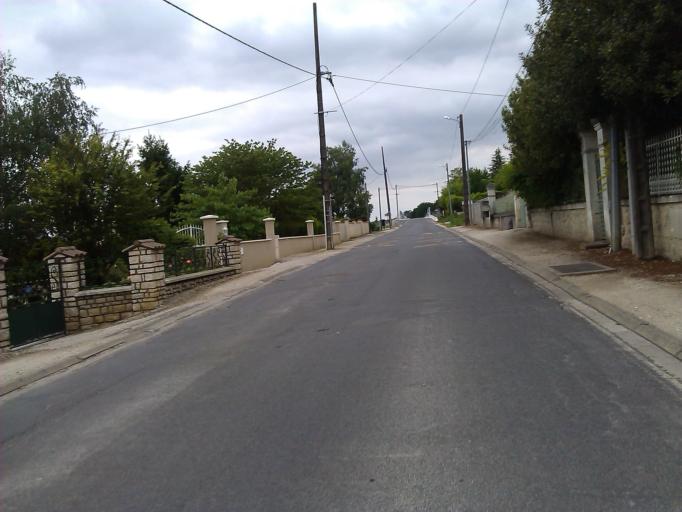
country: FR
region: Poitou-Charentes
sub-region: Departement de la Charente
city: Linars
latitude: 45.6492
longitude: 0.0735
